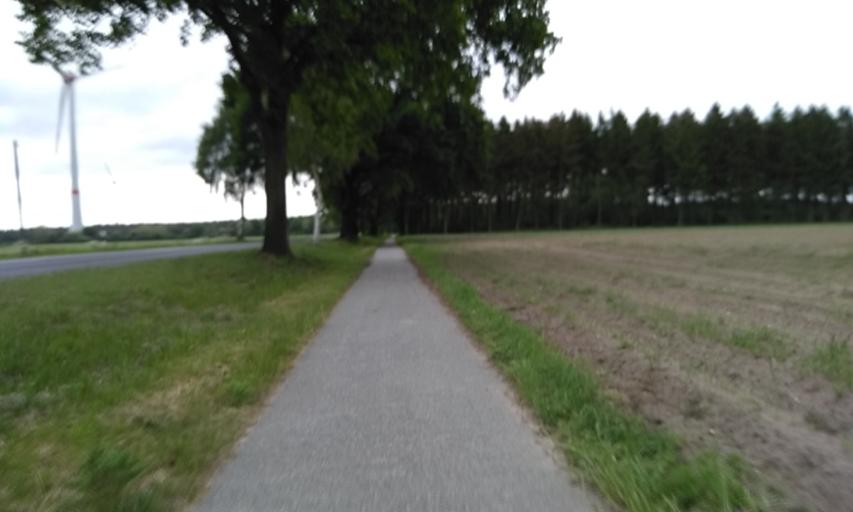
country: DE
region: Lower Saxony
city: Harsefeld
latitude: 53.4878
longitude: 9.4926
